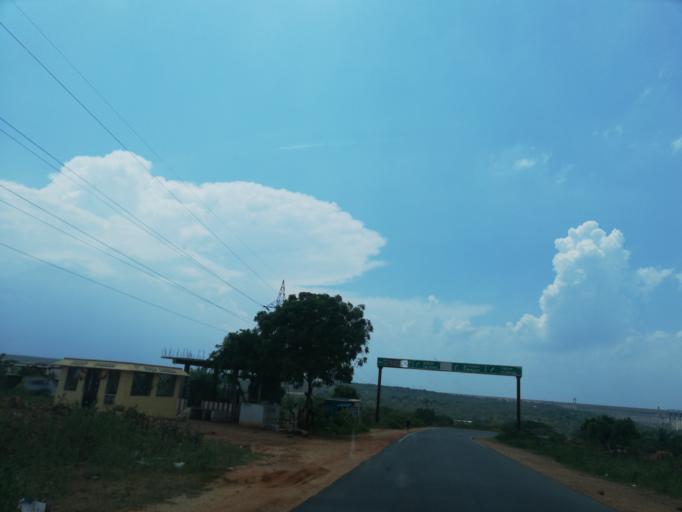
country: IN
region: Andhra Pradesh
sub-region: Guntur
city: Macherla
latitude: 16.5664
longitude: 79.3350
